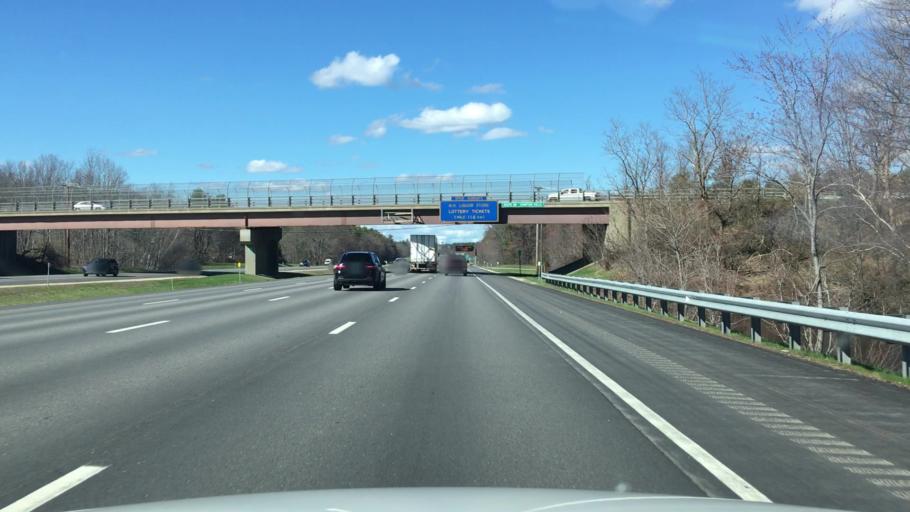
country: US
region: New Hampshire
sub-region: Rockingham County
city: Hampton Falls
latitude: 42.9194
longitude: -70.8700
